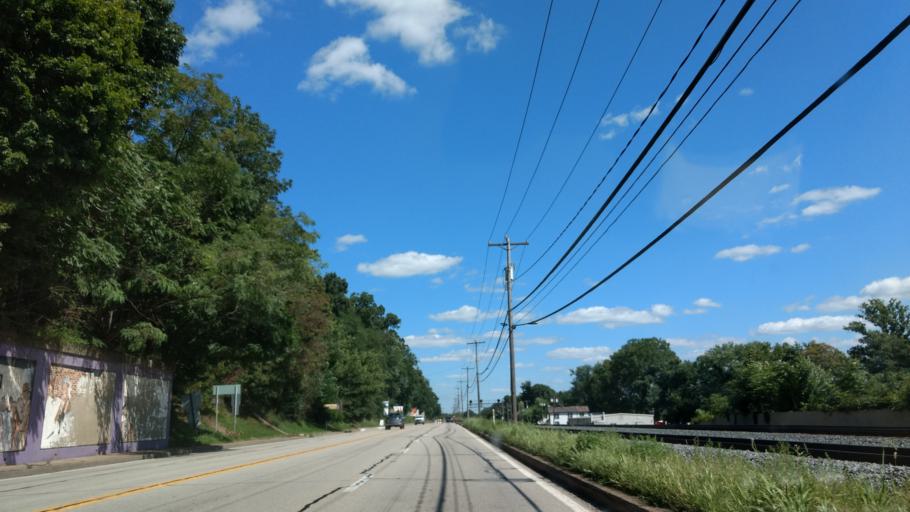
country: US
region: Pennsylvania
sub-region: Allegheny County
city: Coraopolis
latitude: 40.5259
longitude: -80.1577
